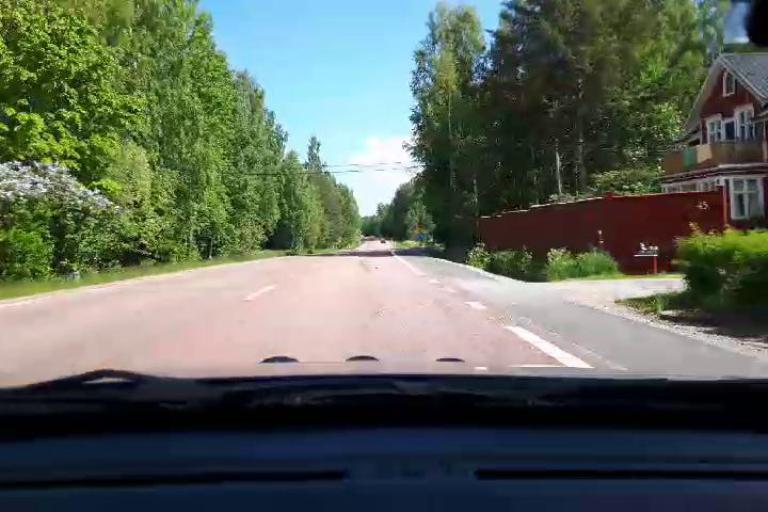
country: SE
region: Gaevleborg
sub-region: Hudiksvalls Kommun
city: Delsbo
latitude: 61.8040
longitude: 16.4672
